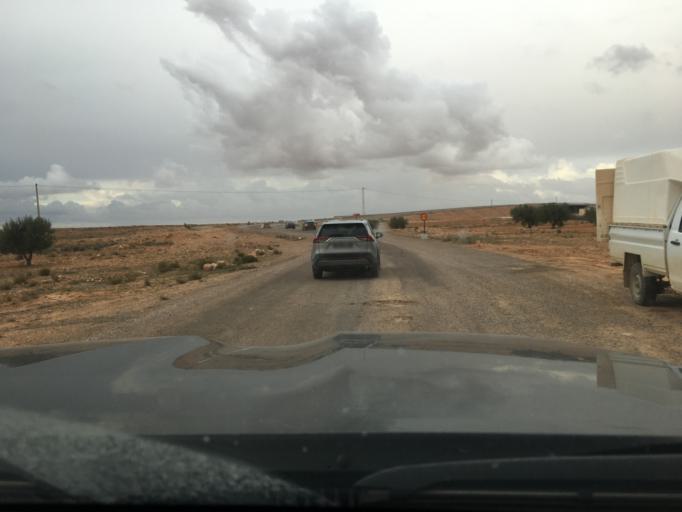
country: TN
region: Madanin
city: Medenine
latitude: 33.2965
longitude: 10.6091
